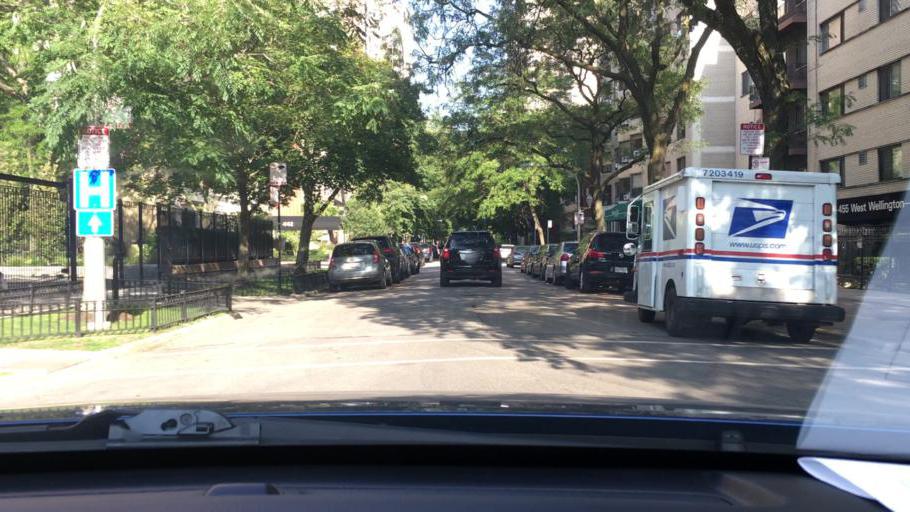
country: US
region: Illinois
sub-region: Cook County
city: Chicago
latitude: 41.9366
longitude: -87.6419
